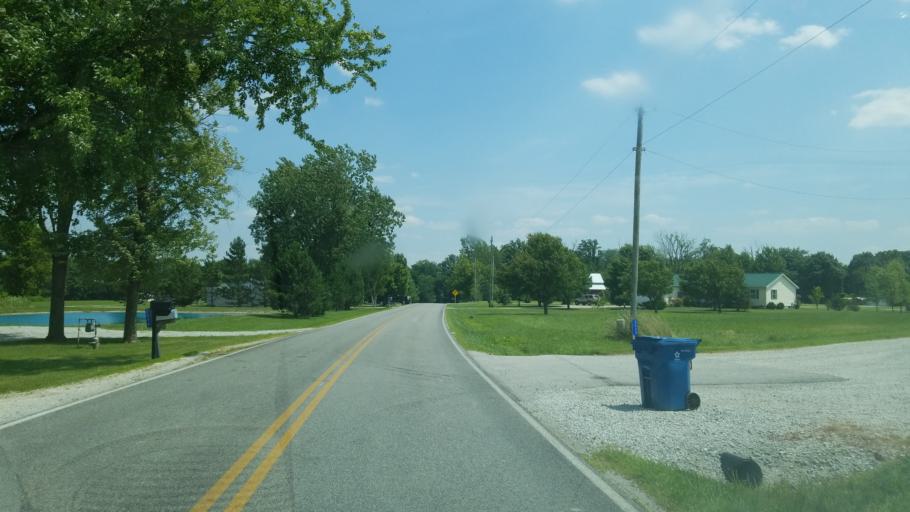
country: US
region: Ohio
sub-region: Seneca County
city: Tiffin
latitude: 41.1624
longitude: -83.2088
